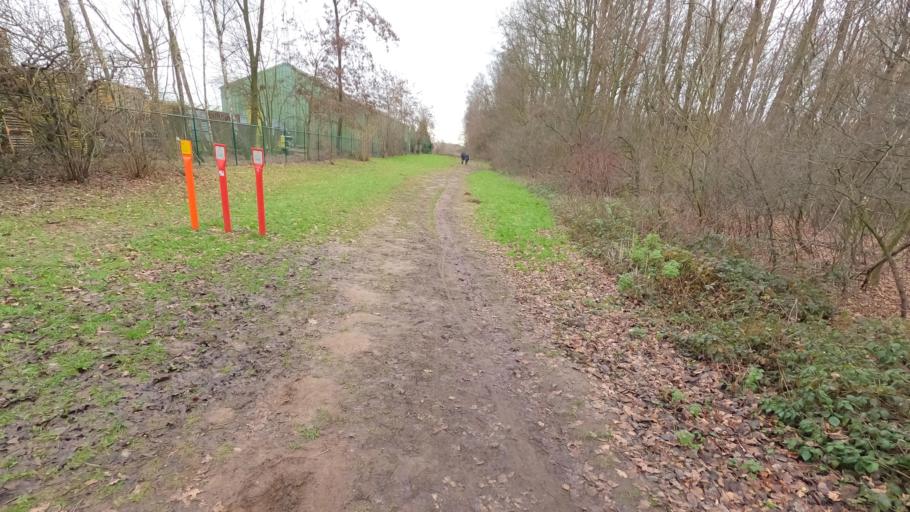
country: BE
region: Flanders
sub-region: Provincie Antwerpen
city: Schoten
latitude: 51.2320
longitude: 4.4915
